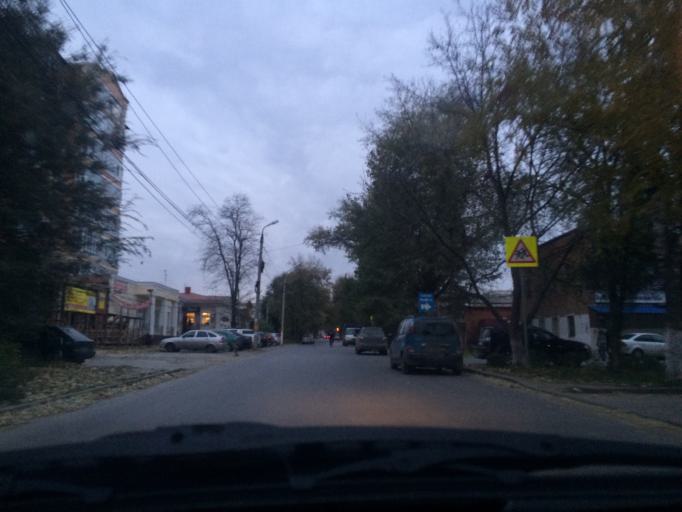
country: RU
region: Rostov
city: Novocherkassk
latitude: 47.4188
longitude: 40.0945
